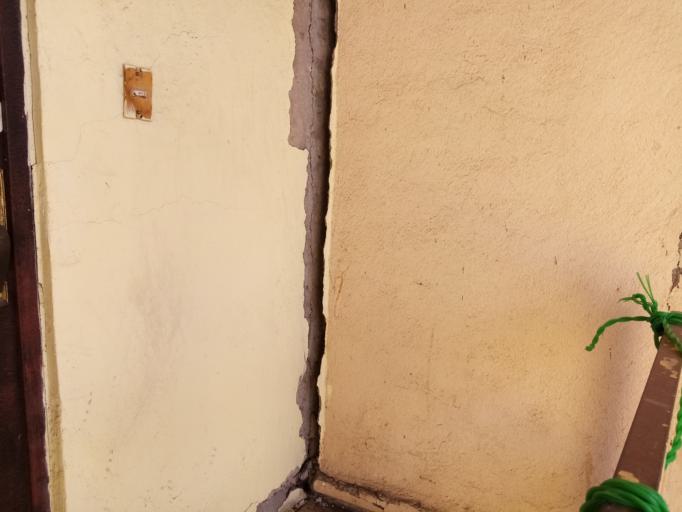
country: MX
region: Mexico City
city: Tlahuac
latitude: 19.2870
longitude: -99.0531
